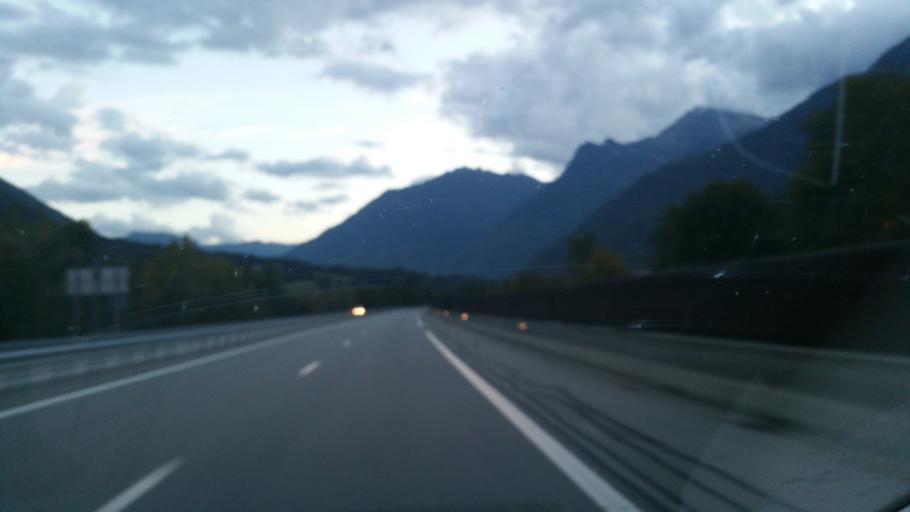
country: FR
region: Rhone-Alpes
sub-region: Departement de la Savoie
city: Saint-Remy-de-Maurienne
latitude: 45.4400
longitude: 6.2836
